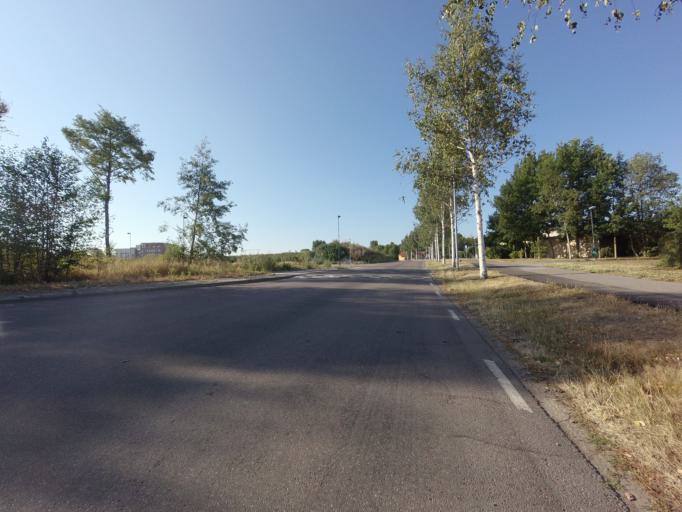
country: SE
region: Skane
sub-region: Landskrona
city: Landskrona
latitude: 55.8989
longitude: 12.8226
